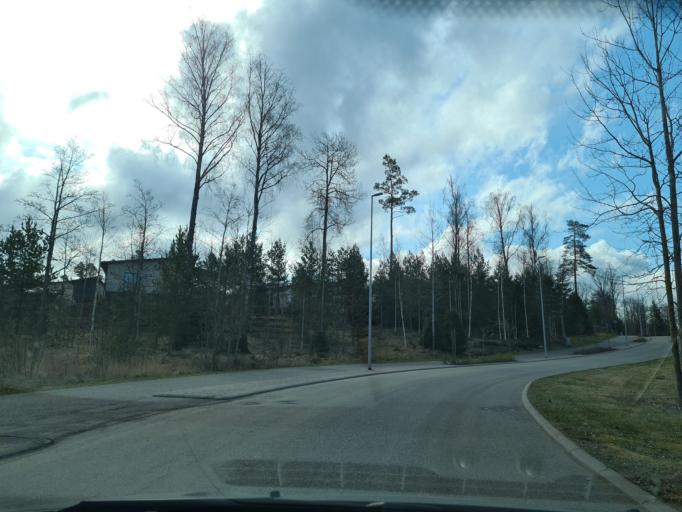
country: FI
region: Uusimaa
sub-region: Helsinki
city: Kirkkonummi
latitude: 60.0801
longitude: 24.4004
